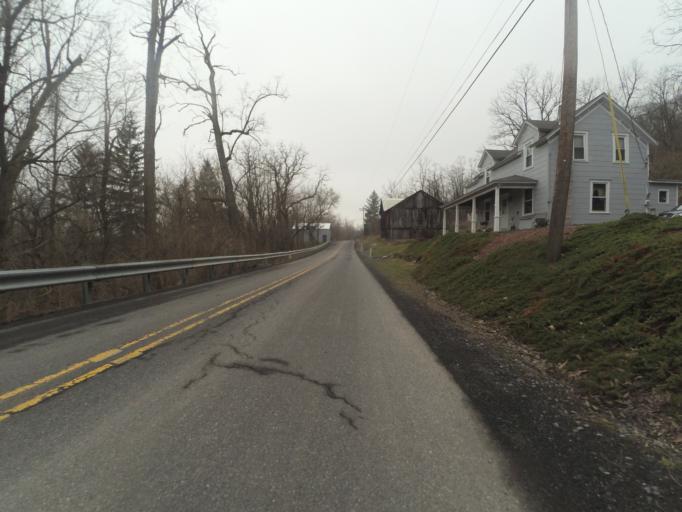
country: US
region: Pennsylvania
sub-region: Centre County
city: Centre Hall
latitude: 40.8328
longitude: -77.5886
